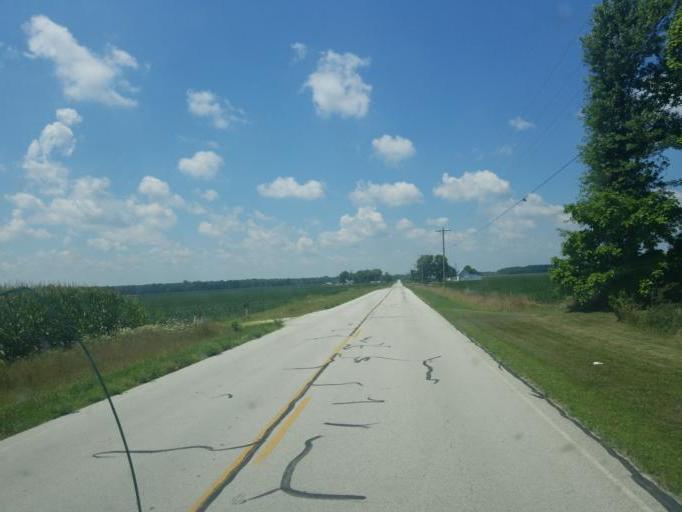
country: US
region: Ohio
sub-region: Allen County
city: Spencerville
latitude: 40.6772
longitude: -84.4821
